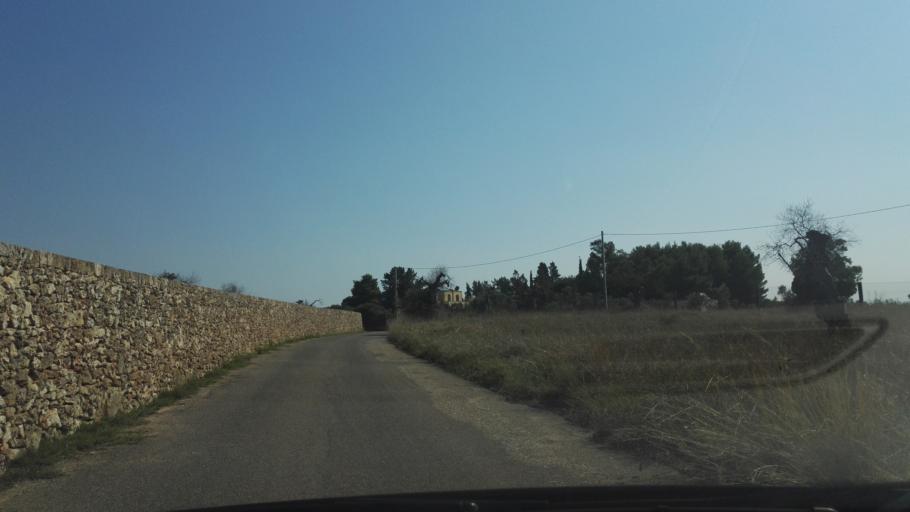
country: IT
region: Apulia
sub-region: Provincia di Lecce
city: Alezio
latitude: 40.0540
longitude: 18.0488
